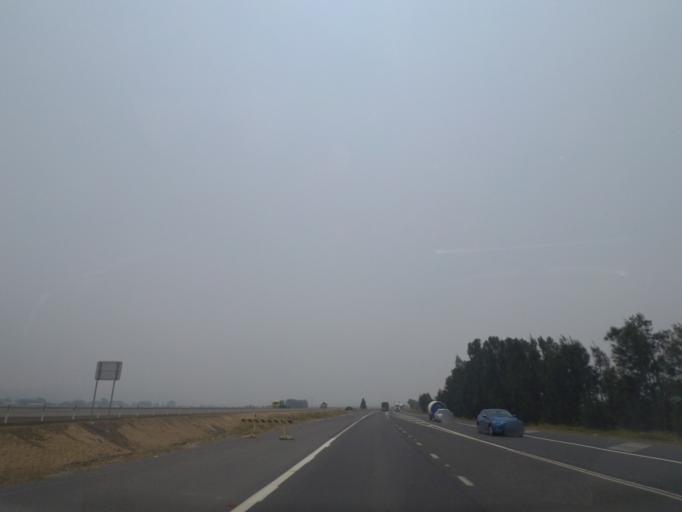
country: AU
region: New South Wales
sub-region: Clarence Valley
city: Maclean
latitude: -29.3913
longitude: 153.2400
